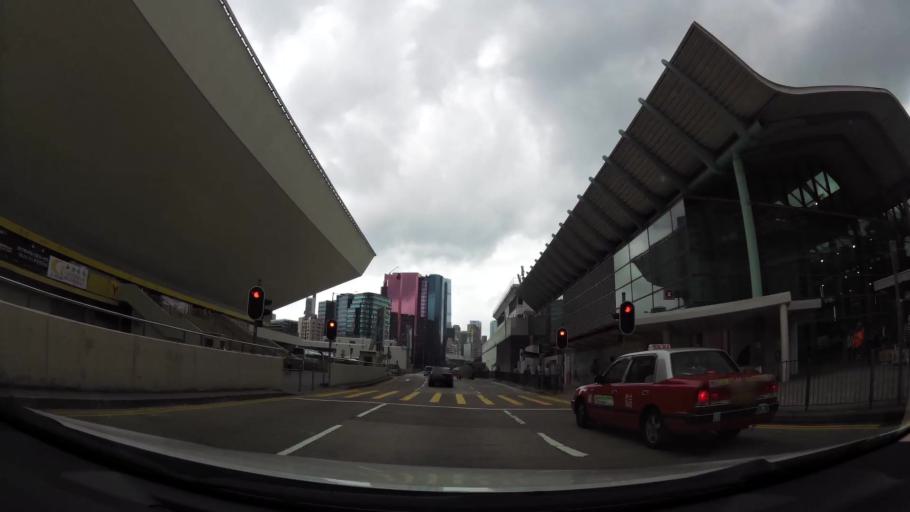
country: HK
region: Kowloon City
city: Kowloon
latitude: 22.3020
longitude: 114.1824
